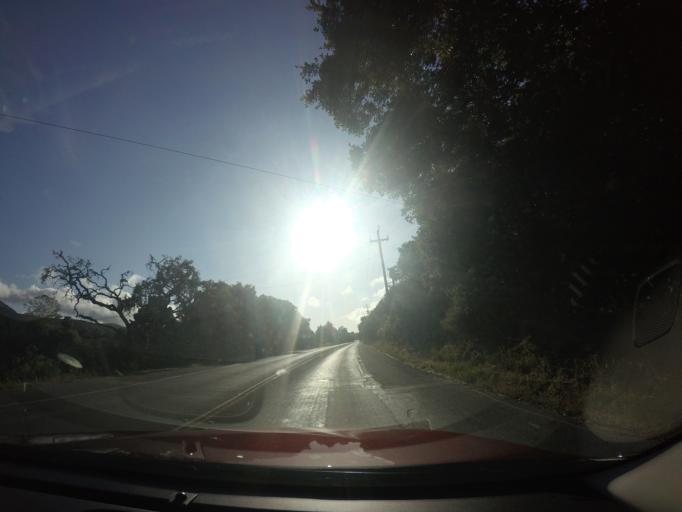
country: US
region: California
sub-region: Monterey County
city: Del Rey Oaks
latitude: 36.5323
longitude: -121.8400
